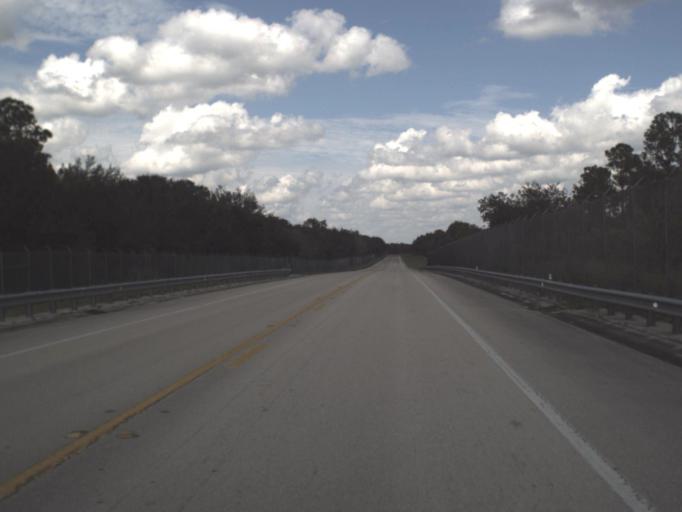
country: US
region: Florida
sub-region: Collier County
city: Immokalee
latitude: 26.1958
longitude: -81.3460
